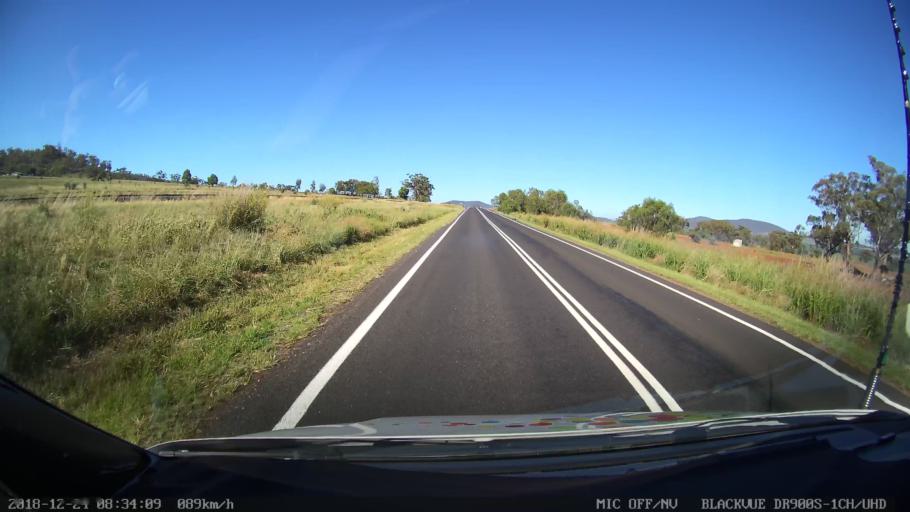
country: AU
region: New South Wales
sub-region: Liverpool Plains
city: Quirindi
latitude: -31.2908
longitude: 150.6746
